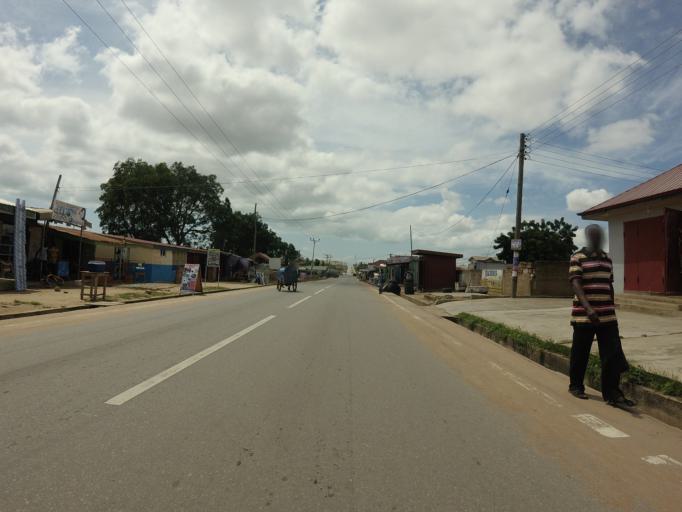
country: GH
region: Central
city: Kasoa
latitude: 5.5364
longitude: -0.4009
